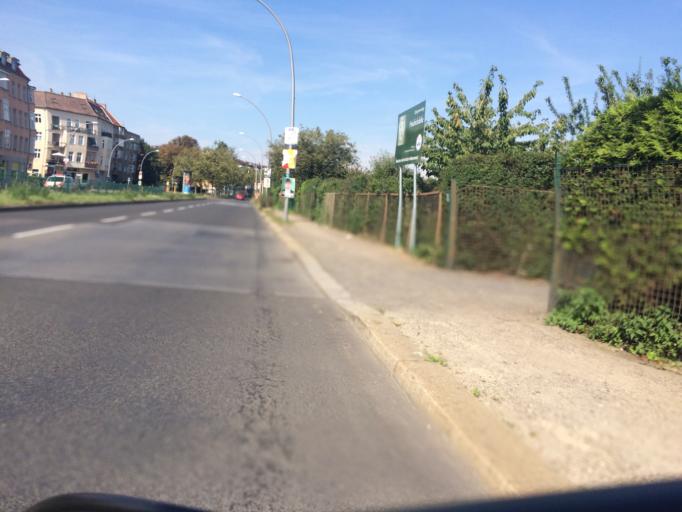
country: DE
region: Berlin
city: Heinersdorf
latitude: 52.5632
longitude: 13.4273
